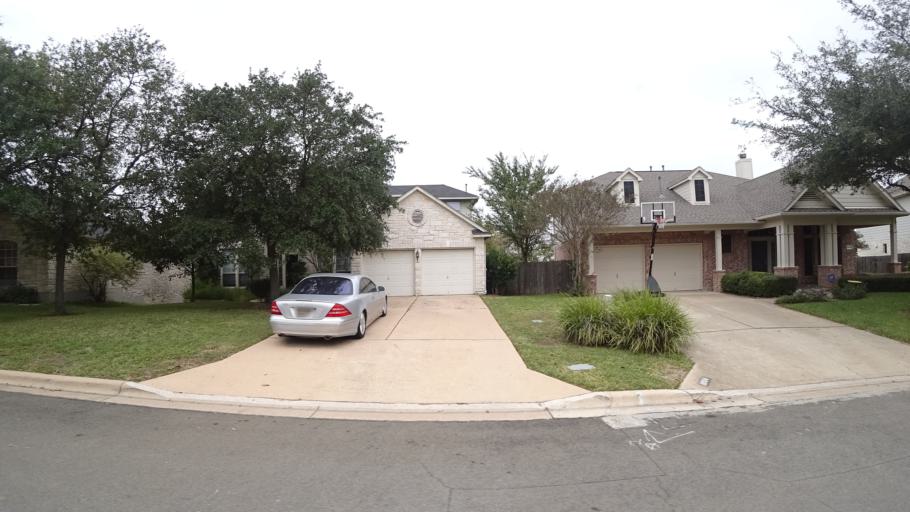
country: US
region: Texas
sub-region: Travis County
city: Shady Hollow
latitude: 30.2159
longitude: -97.8883
